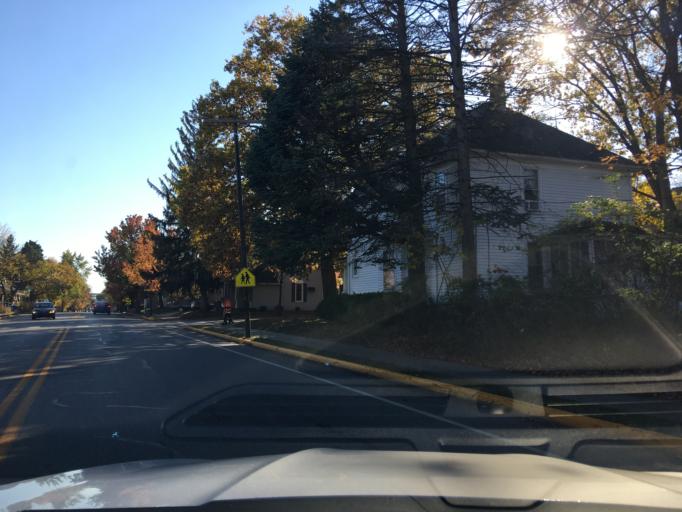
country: US
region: Indiana
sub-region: Tippecanoe County
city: West Lafayette
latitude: 40.4317
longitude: -86.9105
